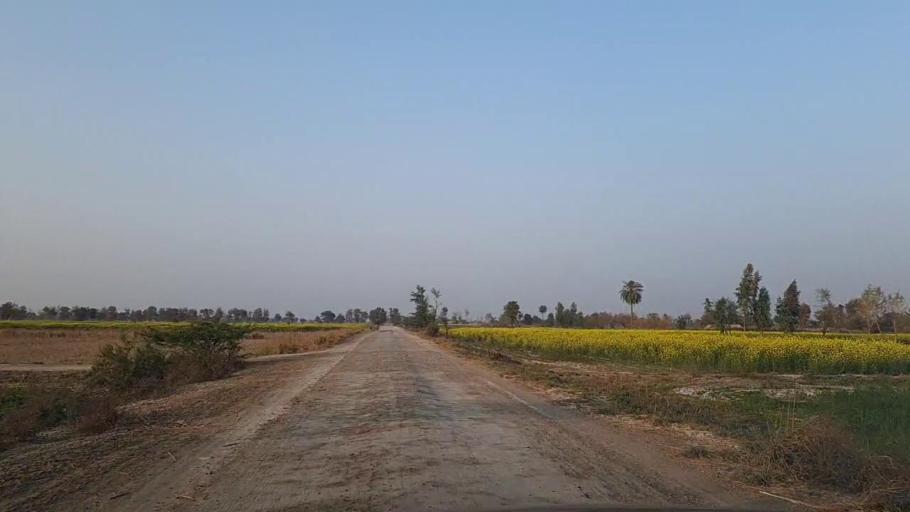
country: PK
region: Sindh
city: Daur
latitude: 26.4264
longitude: 68.3859
